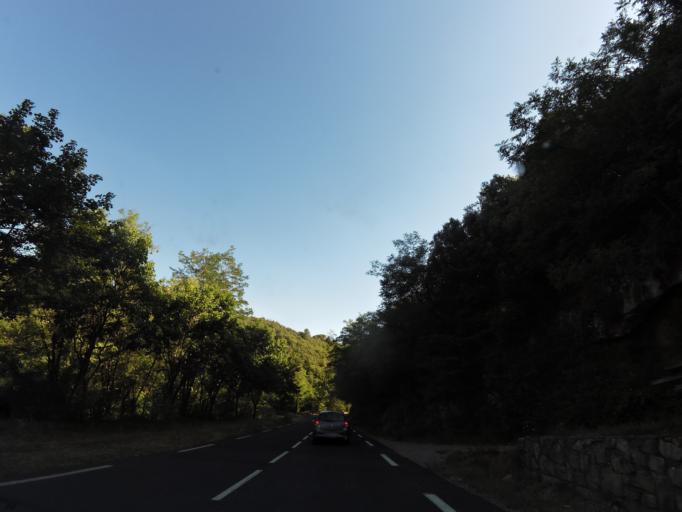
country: FR
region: Languedoc-Roussillon
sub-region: Departement du Gard
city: Valleraugue
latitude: 44.0442
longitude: 3.6753
